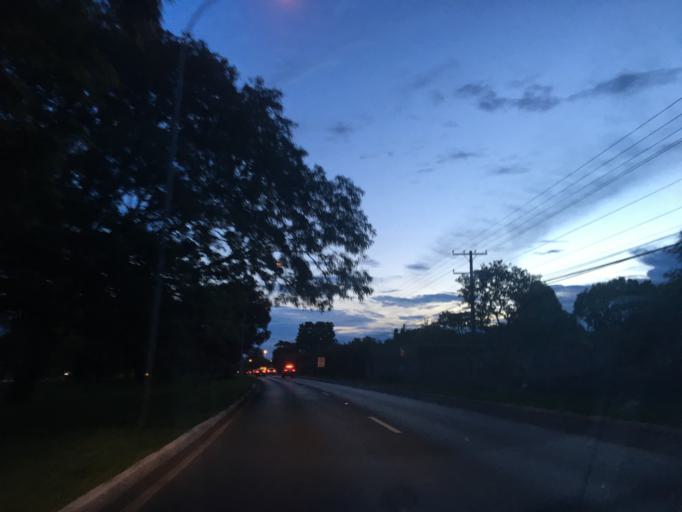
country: BR
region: Federal District
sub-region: Brasilia
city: Brasilia
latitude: -15.8487
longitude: -47.8752
